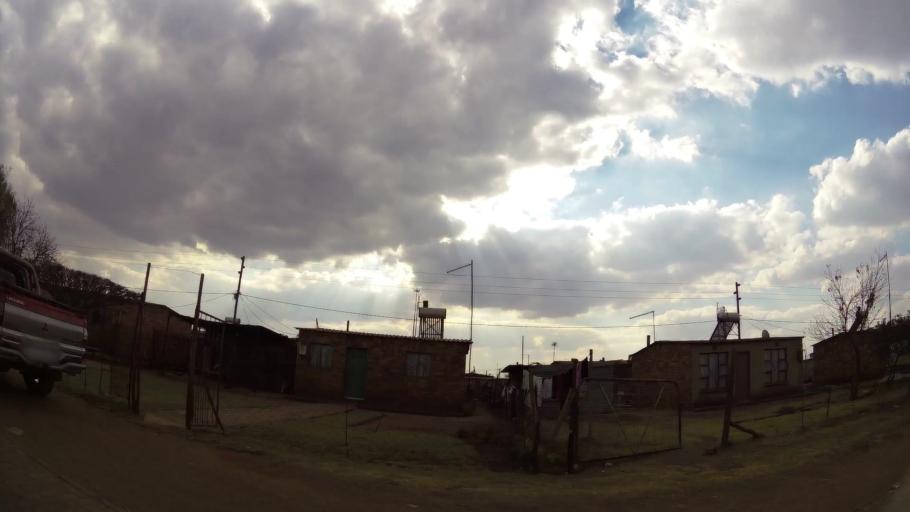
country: ZA
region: Mpumalanga
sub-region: Nkangala District Municipality
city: Delmas
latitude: -26.1406
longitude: 28.6941
